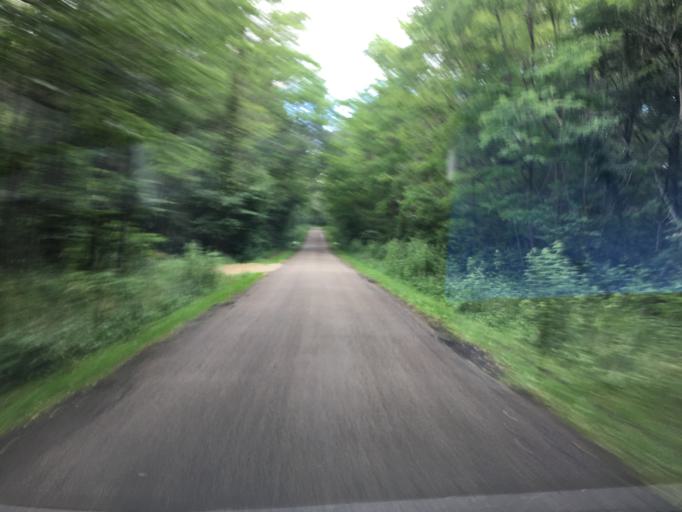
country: FR
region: Bourgogne
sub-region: Departement de l'Yonne
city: Charbuy
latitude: 47.8508
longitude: 3.4891
